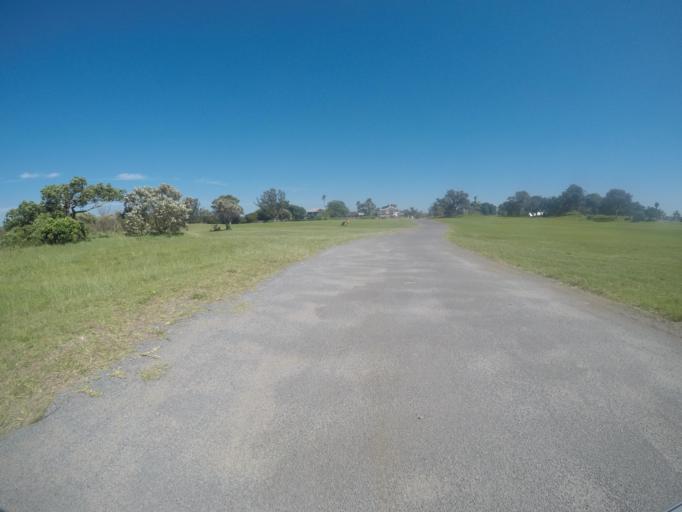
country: ZA
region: Eastern Cape
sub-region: Buffalo City Metropolitan Municipality
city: East London
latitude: -32.9507
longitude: 28.0055
